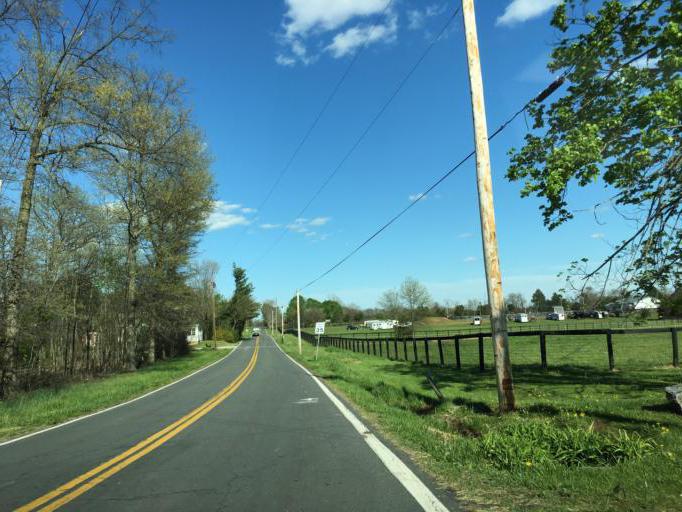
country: US
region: Maryland
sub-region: Frederick County
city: Emmitsburg
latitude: 39.6591
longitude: -77.3302
